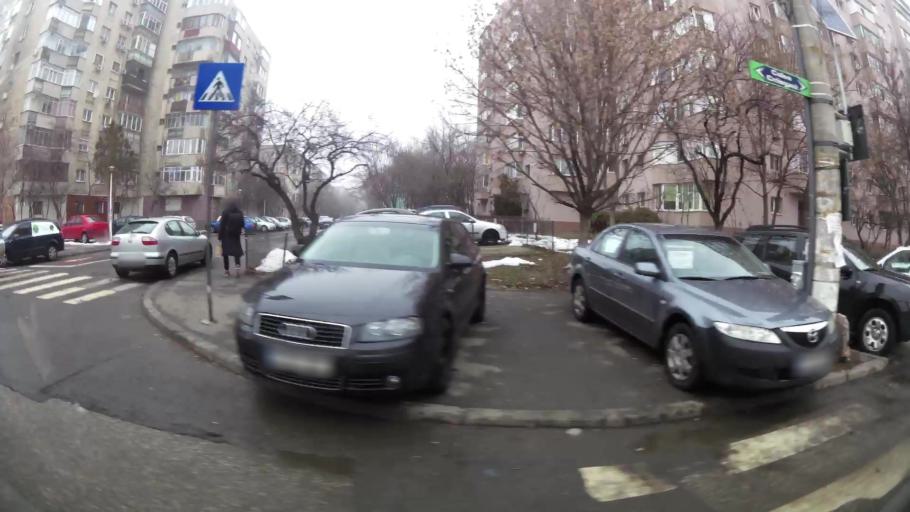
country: RO
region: Ilfov
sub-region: Comuna Chiajna
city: Rosu
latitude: 44.4528
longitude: 26.0437
